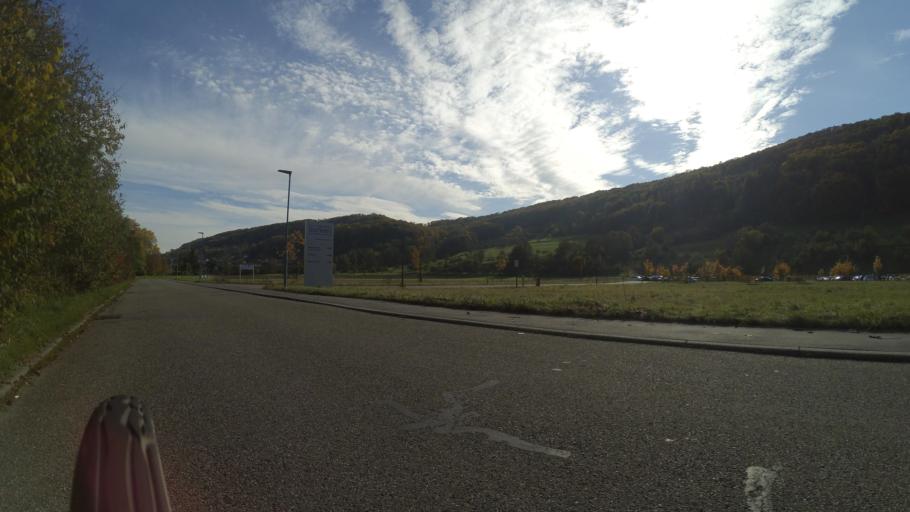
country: DE
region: Baden-Wuerttemberg
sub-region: Regierungsbezirk Stuttgart
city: Ingelfingen
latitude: 49.3000
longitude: 9.6400
